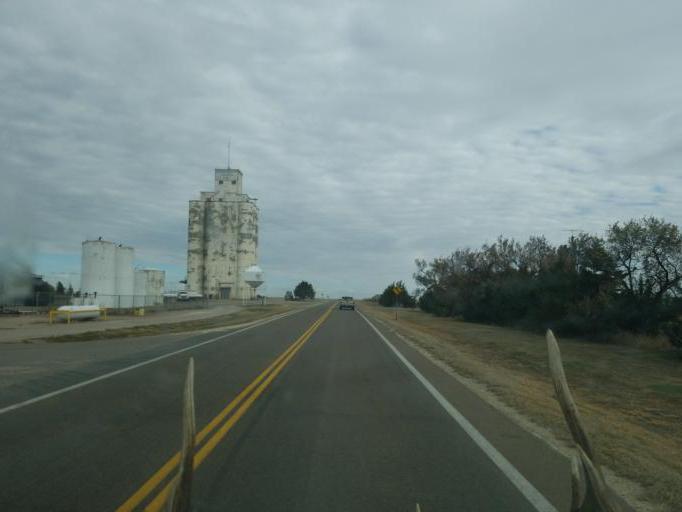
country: US
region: Kansas
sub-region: Logan County
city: Oakley
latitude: 39.0877
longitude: -101.1521
